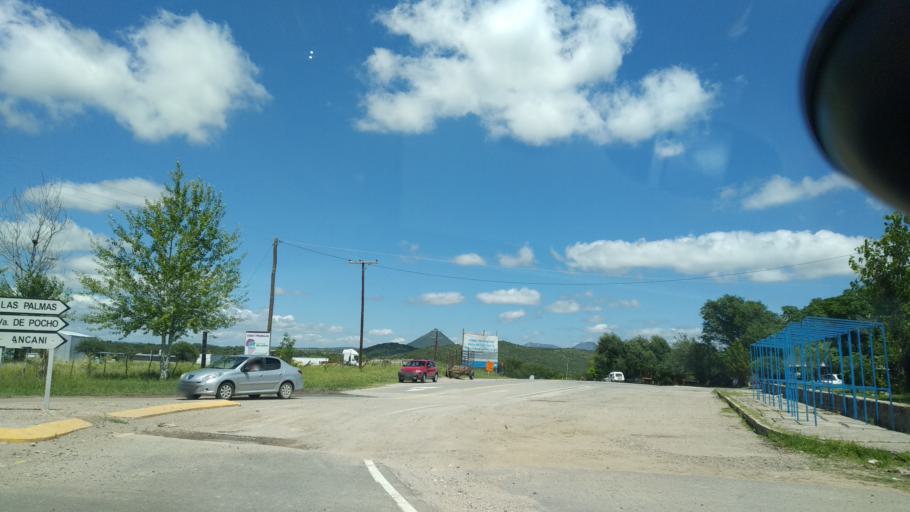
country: AR
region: Cordoba
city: Salsacate
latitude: -31.3461
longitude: -65.0797
